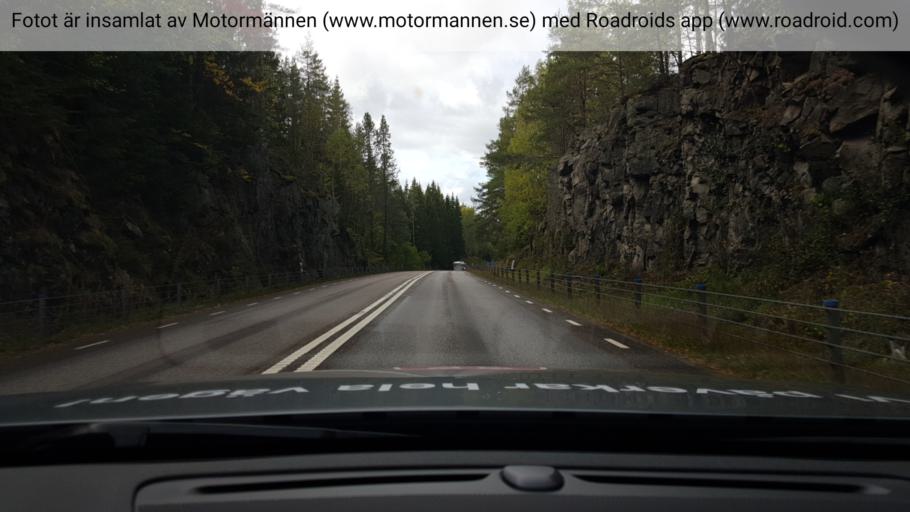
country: SE
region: Vaermland
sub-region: Arjangs Kommun
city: Toecksfors
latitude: 59.4745
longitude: 11.9719
